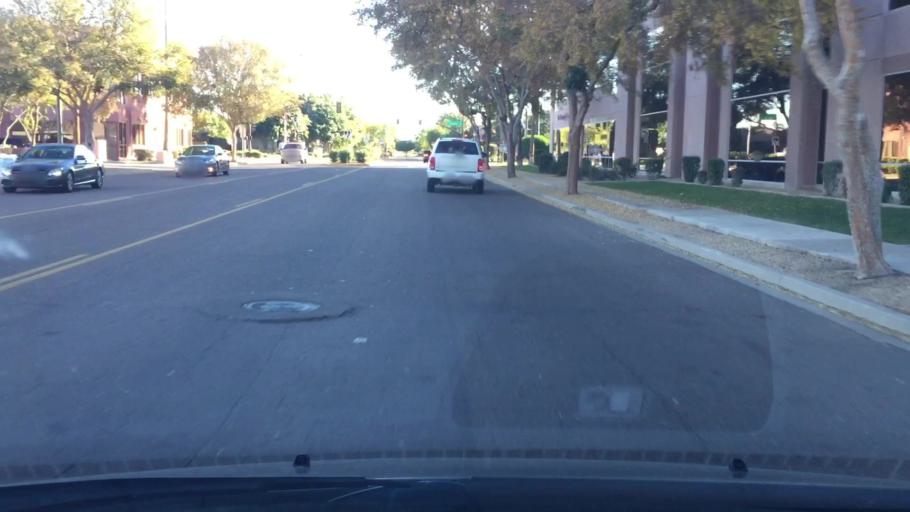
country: US
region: Arizona
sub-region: Maricopa County
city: Gilbert
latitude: 33.3804
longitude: -111.7441
